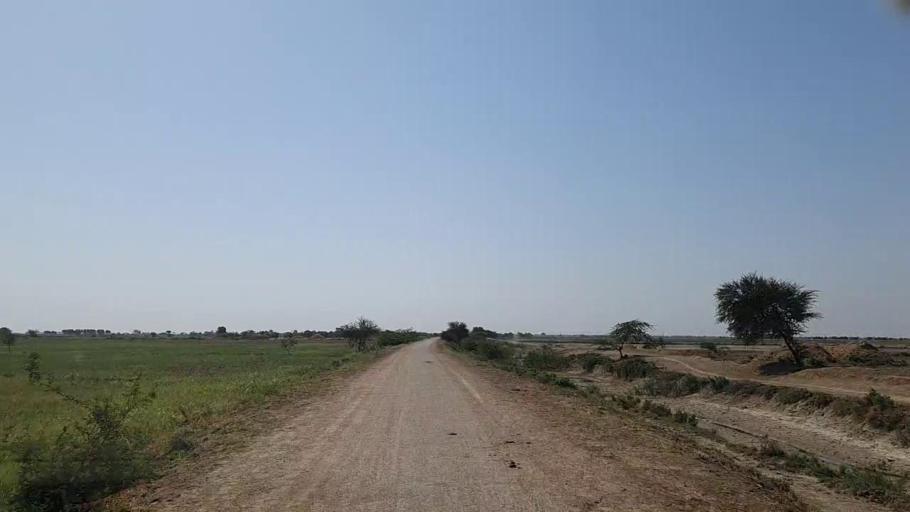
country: PK
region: Sindh
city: Mirpur Batoro
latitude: 24.6773
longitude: 68.3048
